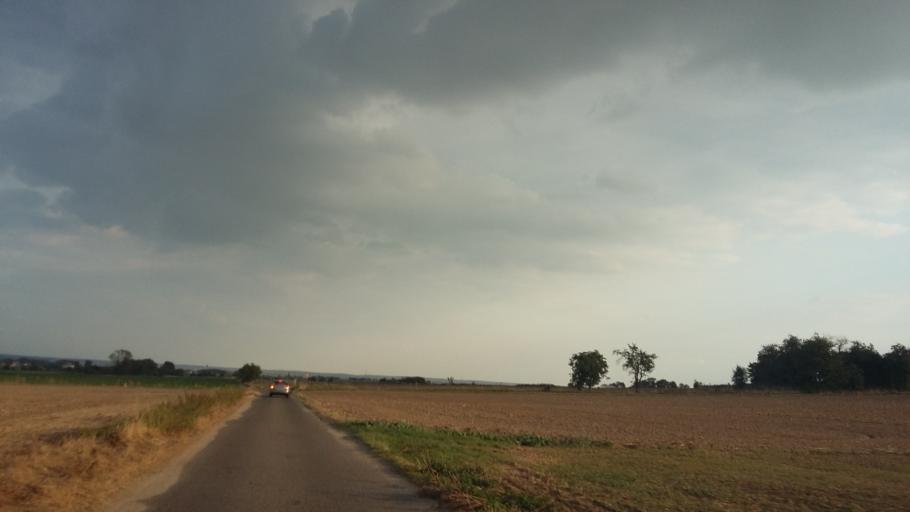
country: CZ
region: Central Bohemia
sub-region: Okres Mlada Boleslav
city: Mlada Boleslav
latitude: 50.3584
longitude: 14.8918
